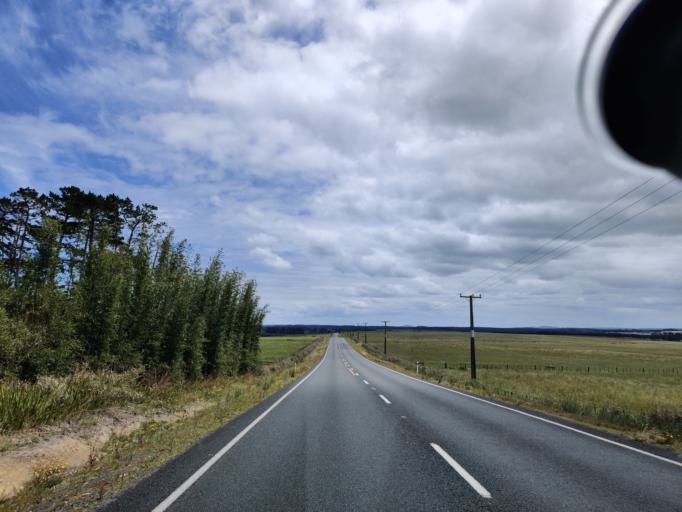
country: NZ
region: Northland
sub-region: Far North District
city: Kaitaia
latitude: -34.6928
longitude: 173.0218
